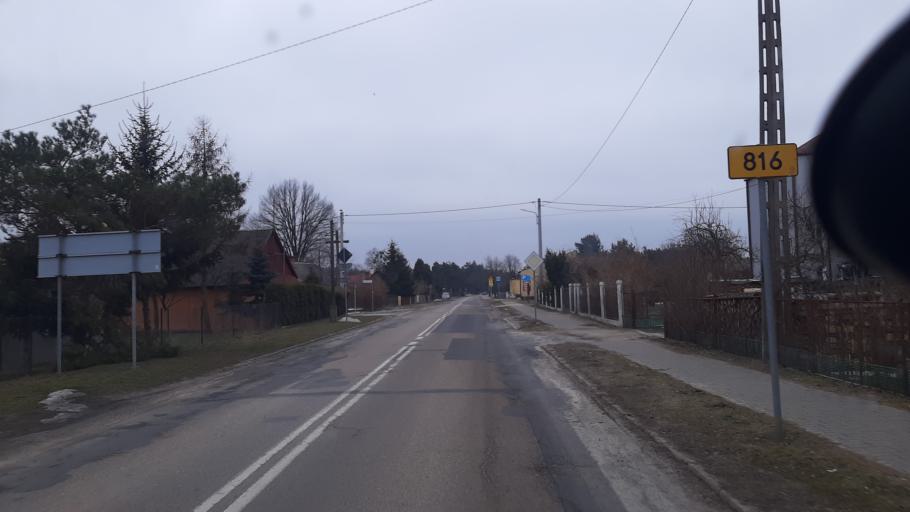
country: PL
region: Lublin Voivodeship
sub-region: Powiat wlodawski
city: Wlodawa
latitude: 51.5232
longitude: 23.5728
